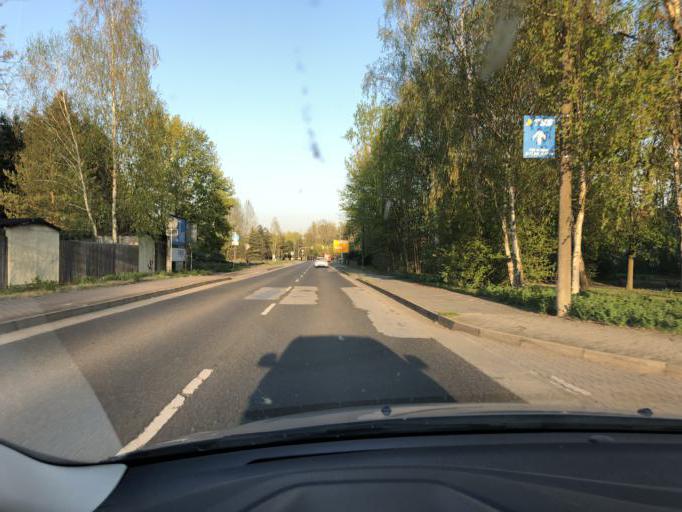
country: DE
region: Brandenburg
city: Spremberg
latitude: 51.5242
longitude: 14.3311
